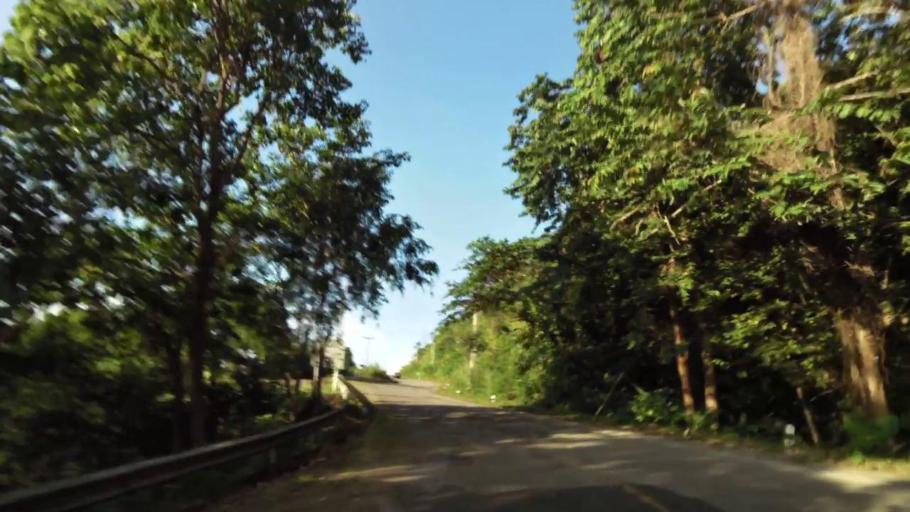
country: TH
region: Chiang Rai
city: Khun Tan
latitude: 19.8639
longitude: 100.4408
